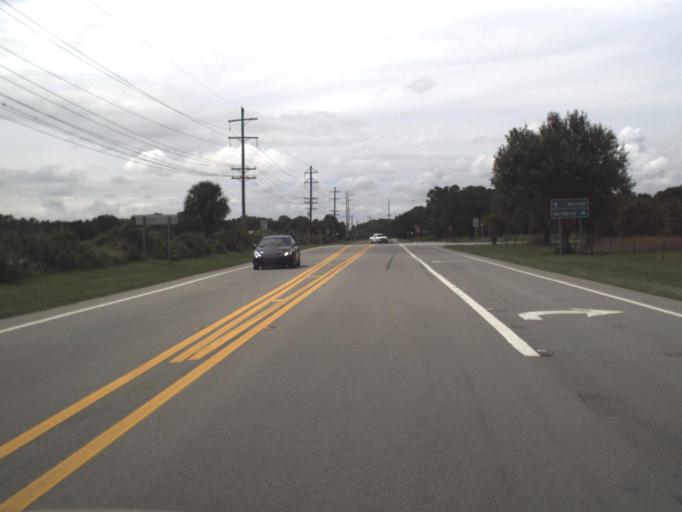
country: US
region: Florida
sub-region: Hillsborough County
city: Wimauma
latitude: 27.5899
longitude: -82.1175
